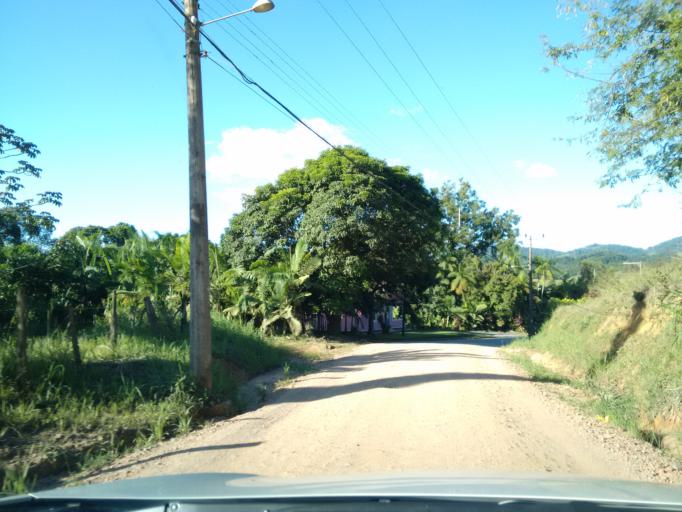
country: BR
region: Santa Catarina
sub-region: Pomerode
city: Pomerode
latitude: -26.7998
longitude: -49.1632
